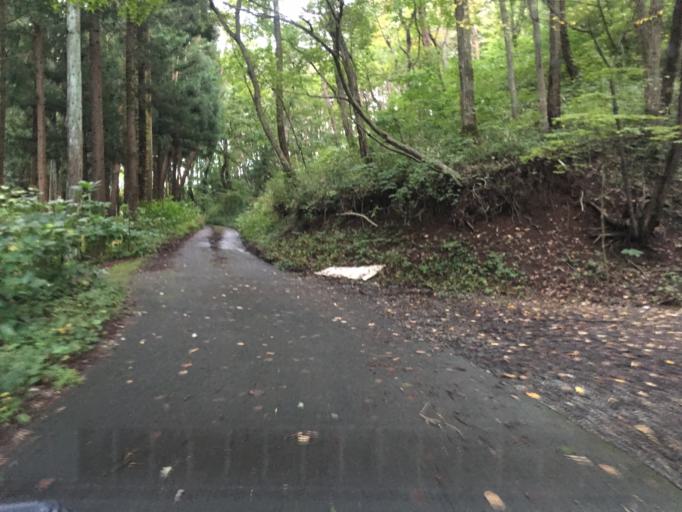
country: JP
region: Fukushima
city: Fukushima-shi
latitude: 37.7544
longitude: 140.5033
